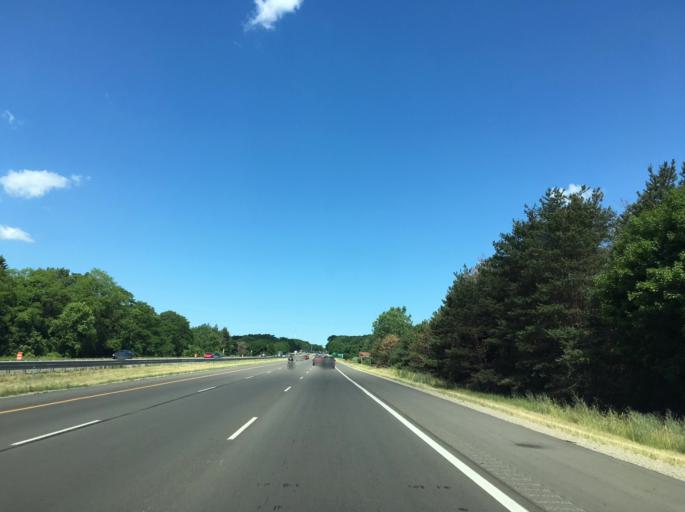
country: US
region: Michigan
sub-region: Oakland County
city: Clarkston
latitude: 42.7269
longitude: -83.3583
